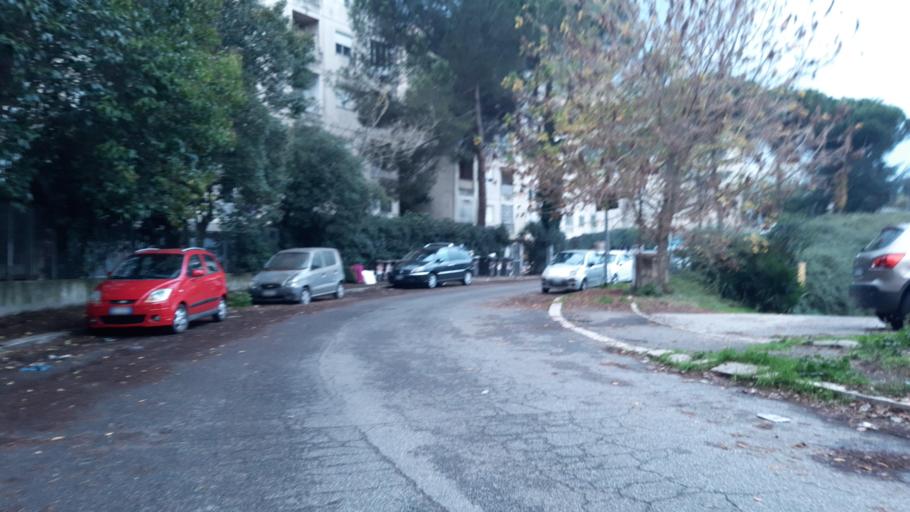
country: VA
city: Vatican City
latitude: 41.9660
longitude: 12.4049
